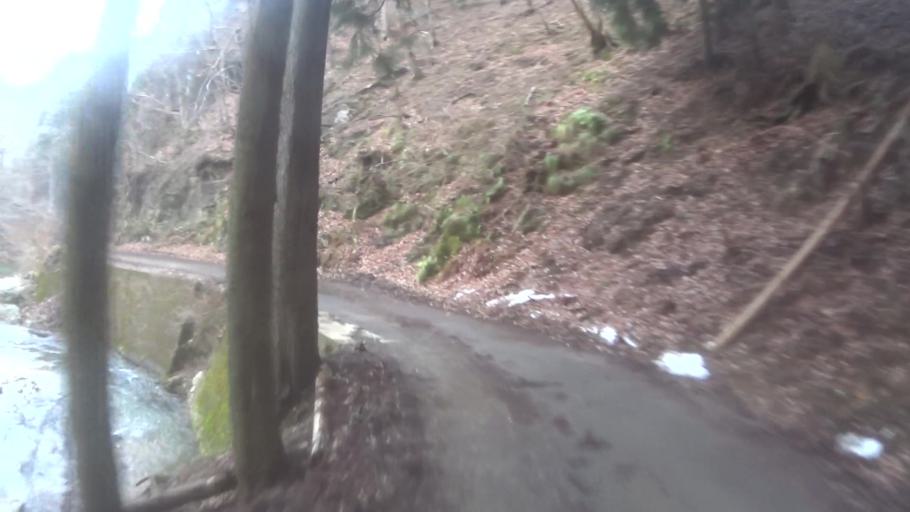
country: JP
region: Kyoto
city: Maizuru
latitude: 35.3995
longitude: 135.4975
